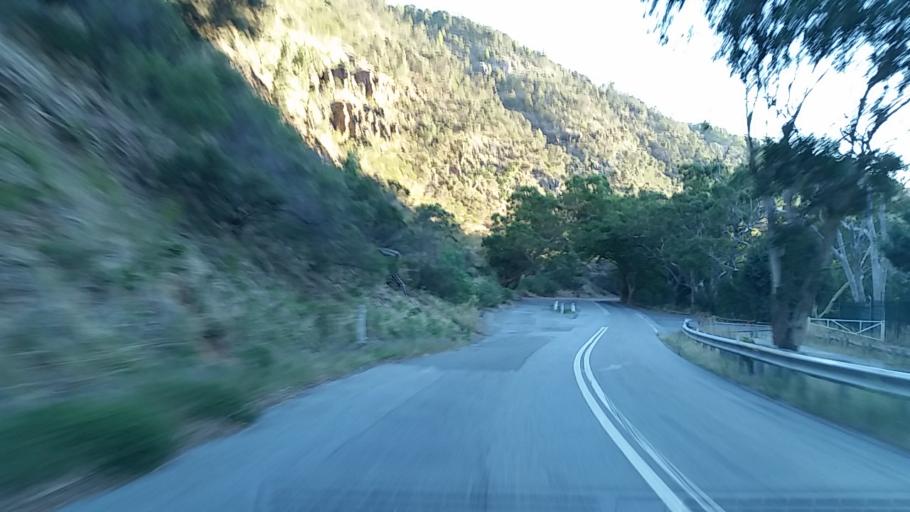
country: AU
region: South Australia
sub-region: Campbelltown
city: Athelstone
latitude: -34.8578
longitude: 138.7308
